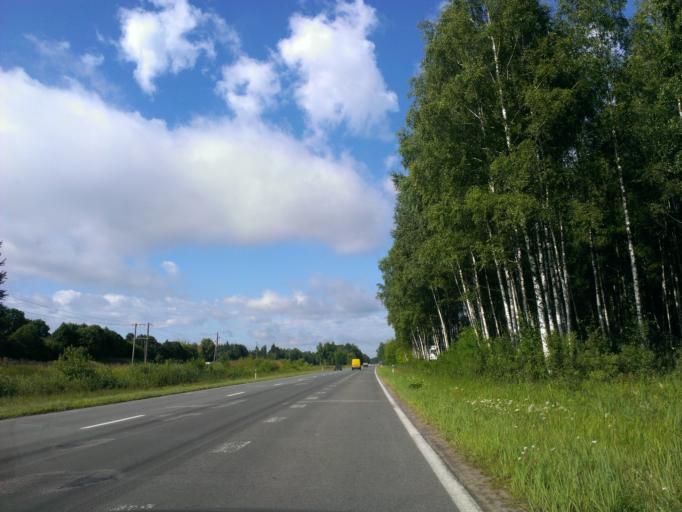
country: LV
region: Incukalns
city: Vangazi
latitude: 57.0895
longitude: 24.5518
